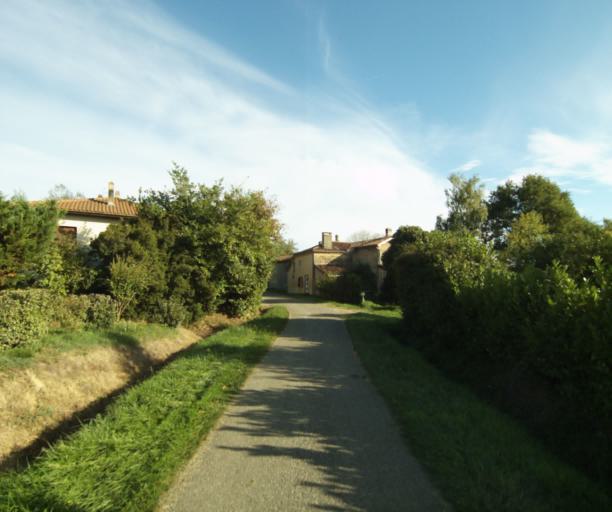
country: FR
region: Midi-Pyrenees
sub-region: Departement du Gers
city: Eauze
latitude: 43.8636
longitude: 0.0283
